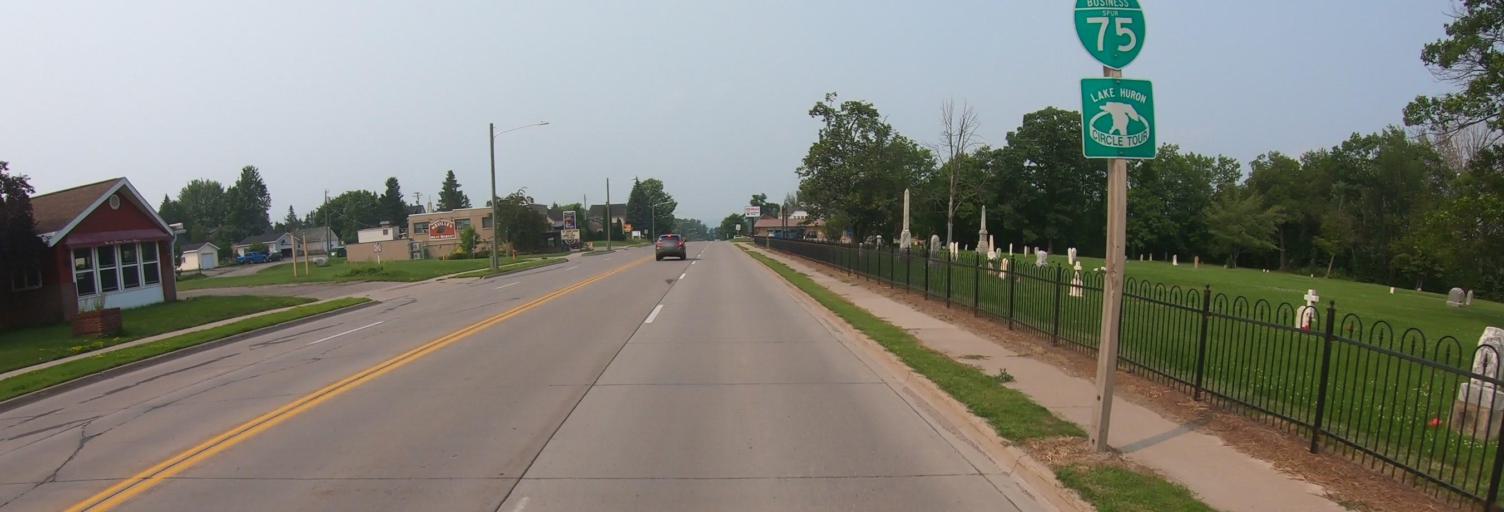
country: US
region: Michigan
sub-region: Chippewa County
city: Sault Ste. Marie
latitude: 46.4848
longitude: -84.3536
